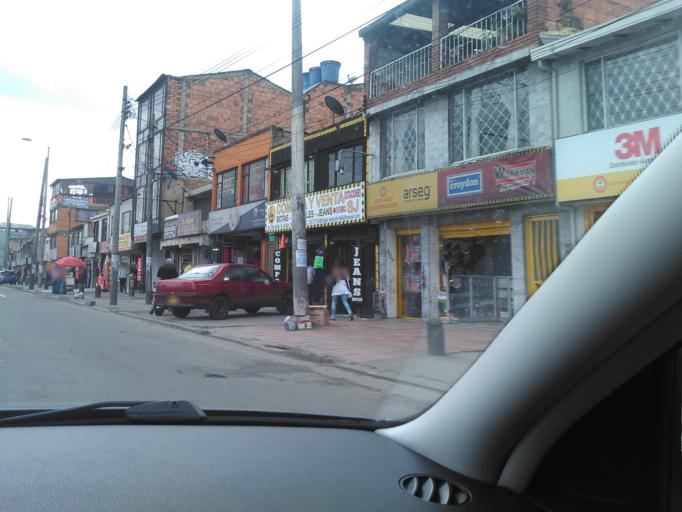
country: CO
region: Bogota D.C.
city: Bogota
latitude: 4.6148
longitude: -74.1272
